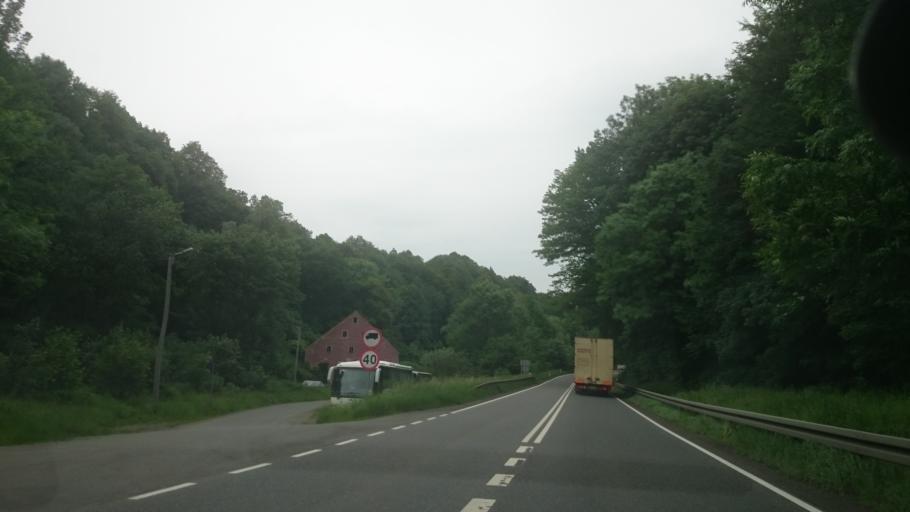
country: PL
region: Lower Silesian Voivodeship
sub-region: Powiat zabkowicki
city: Zloty Stok
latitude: 50.4517
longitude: 16.8404
